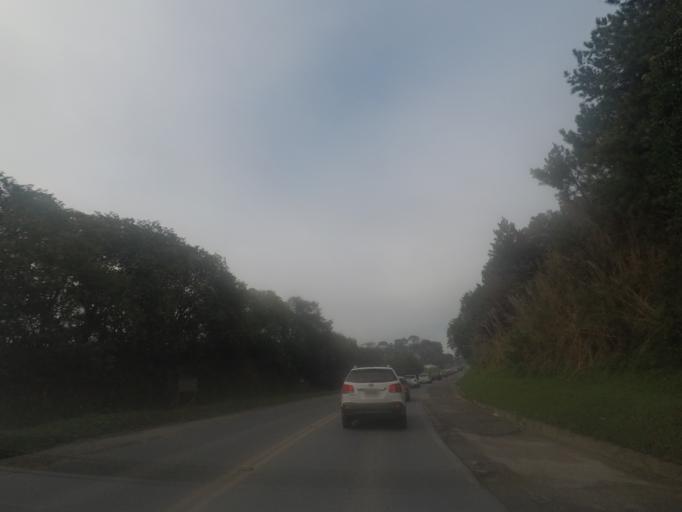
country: BR
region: Parana
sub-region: Almirante Tamandare
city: Almirante Tamandare
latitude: -25.3083
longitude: -49.3036
